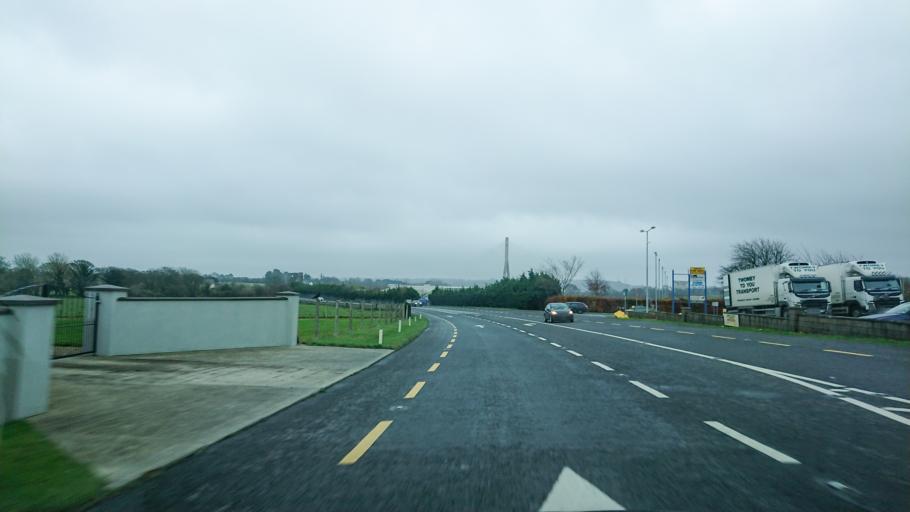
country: IE
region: Munster
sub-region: Waterford
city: Waterford
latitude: 52.2804
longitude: -7.1677
